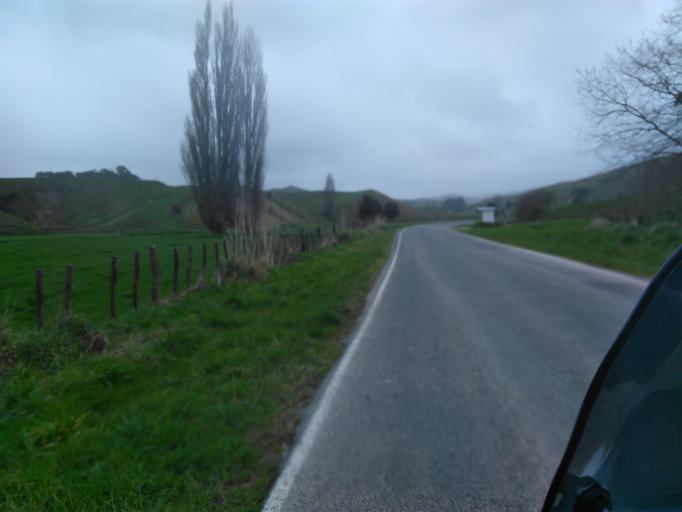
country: NZ
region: Gisborne
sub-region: Gisborne District
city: Gisborne
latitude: -38.6356
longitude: 177.6919
